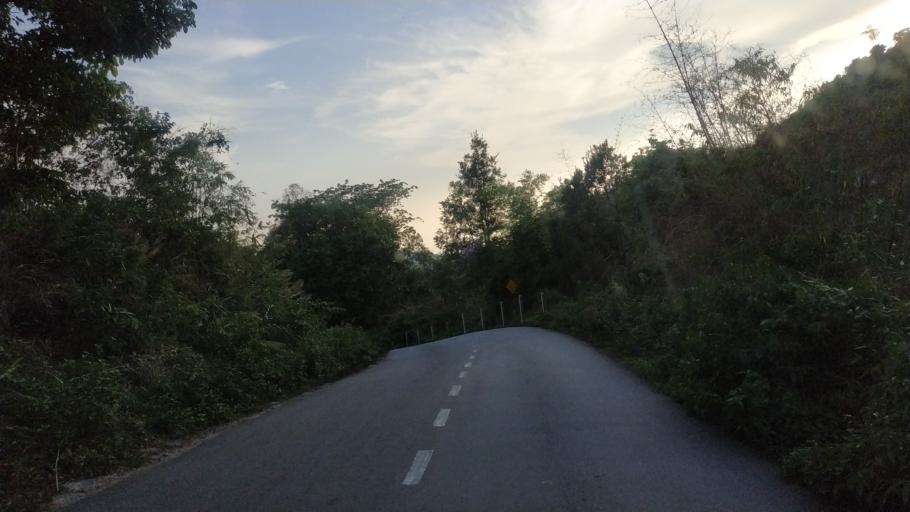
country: MM
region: Mon
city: Kyaikto
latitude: 17.4231
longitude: 97.0750
